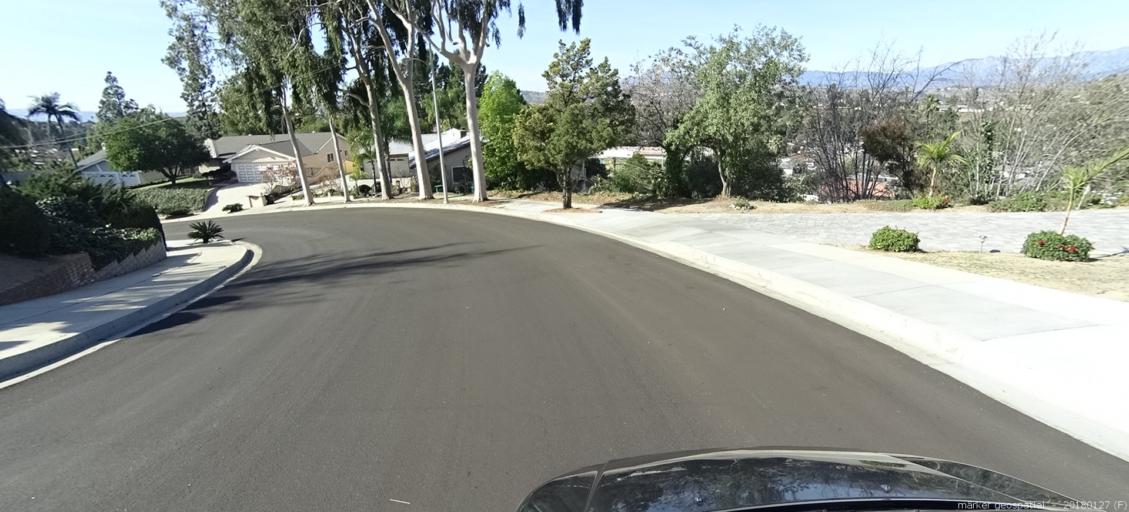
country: US
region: California
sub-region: Los Angeles County
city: Diamond Bar
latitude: 34.0208
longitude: -117.8036
